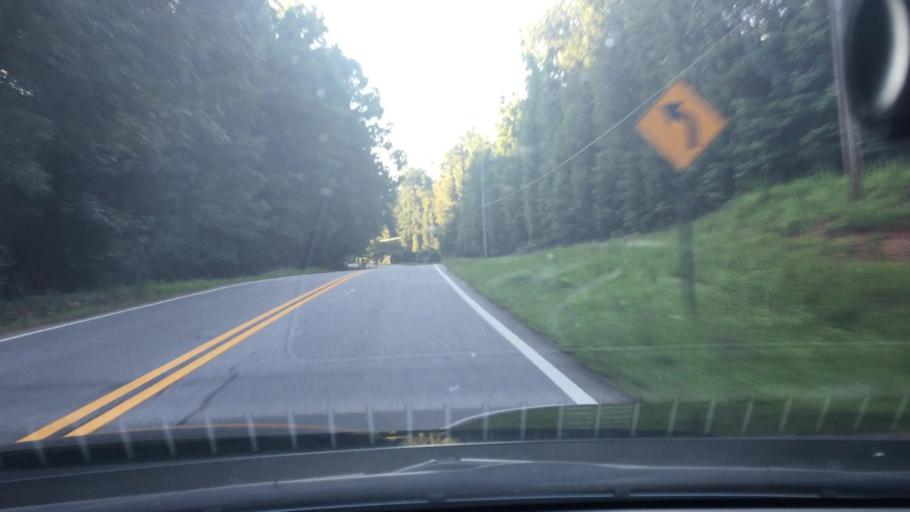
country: US
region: Georgia
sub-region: Coweta County
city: East Newnan
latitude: 33.3470
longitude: -84.7506
